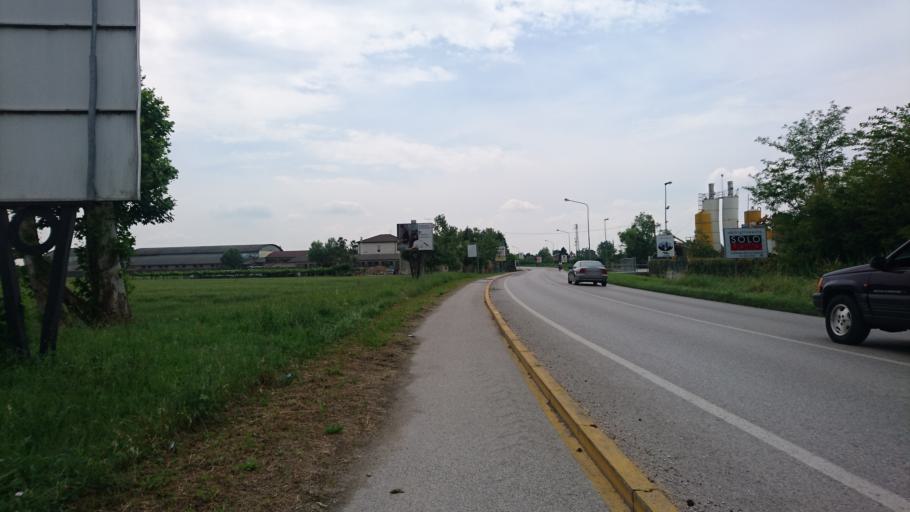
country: IT
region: Veneto
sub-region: Provincia di Rovigo
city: Badia Polesine
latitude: 45.0901
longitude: 11.4825
